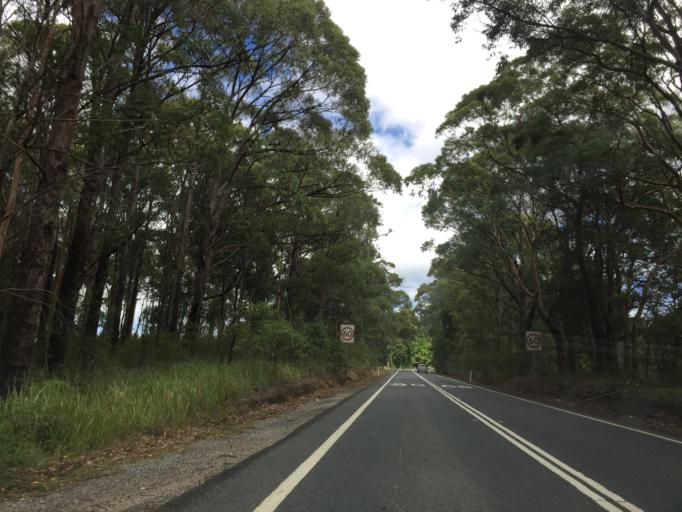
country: AU
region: New South Wales
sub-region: Hawkesbury
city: Richmond
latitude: -33.5096
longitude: 150.5646
